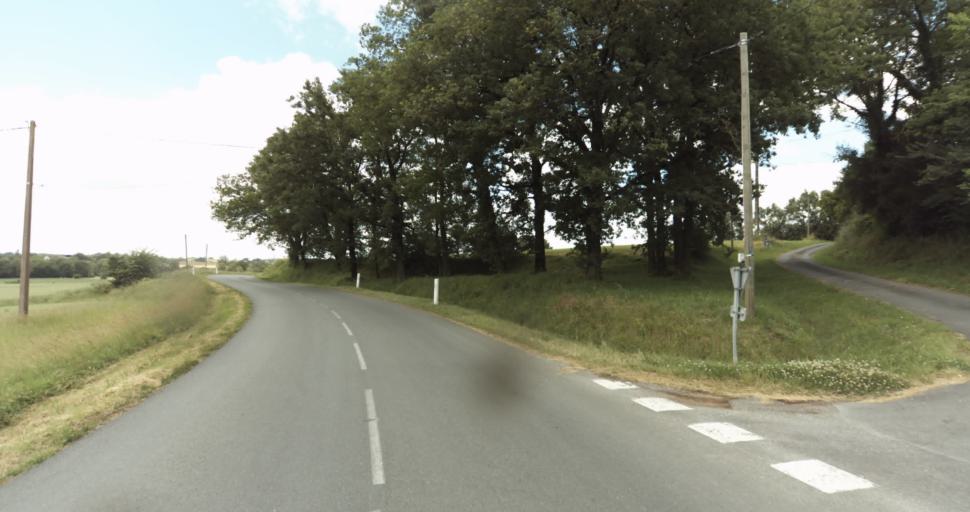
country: FR
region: Aquitaine
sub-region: Departement du Lot-et-Garonne
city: Villereal
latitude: 44.6846
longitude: 0.7575
